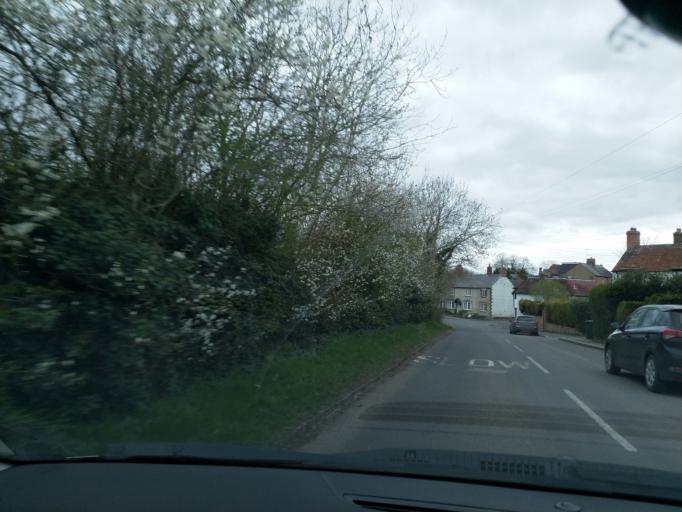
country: GB
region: England
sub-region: Warwickshire
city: Wellesbourne Mountford
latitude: 52.1560
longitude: -1.5044
